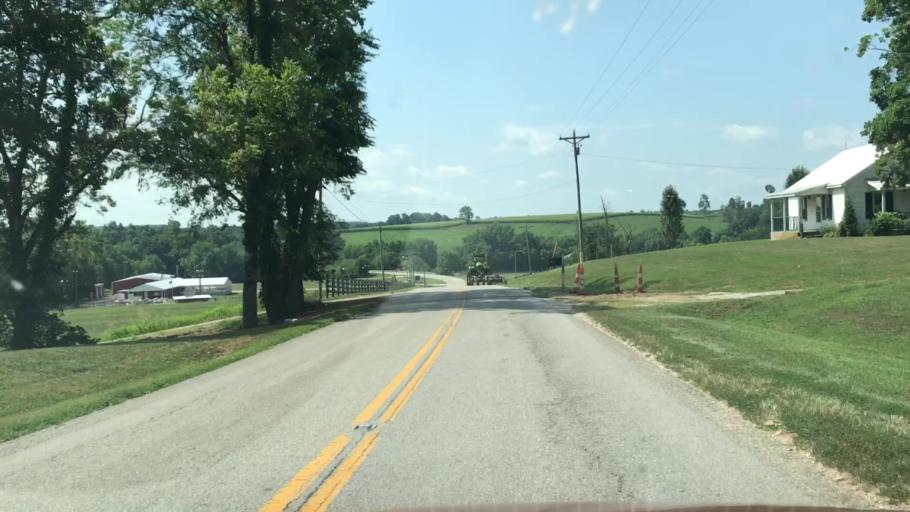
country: US
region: Kentucky
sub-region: Barren County
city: Glasgow
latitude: 36.8700
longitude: -85.8488
